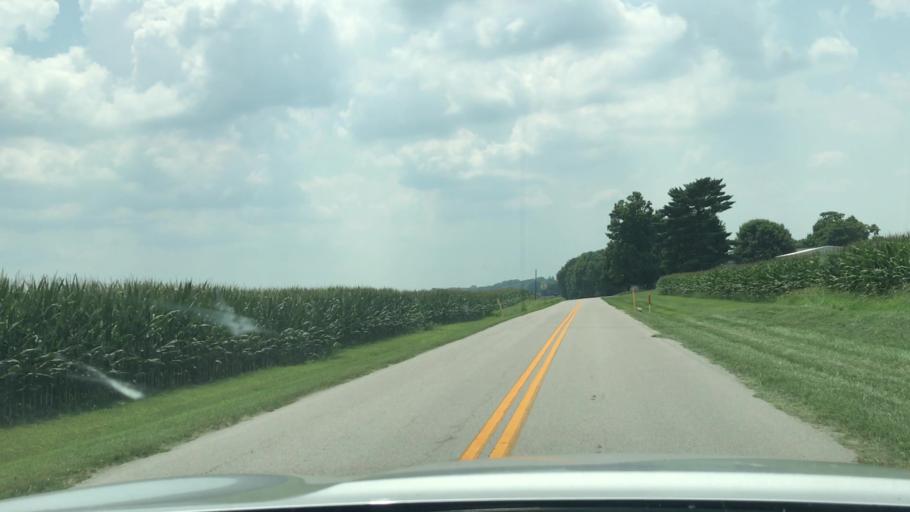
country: US
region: Kentucky
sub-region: Todd County
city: Elkton
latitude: 36.7562
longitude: -87.0963
